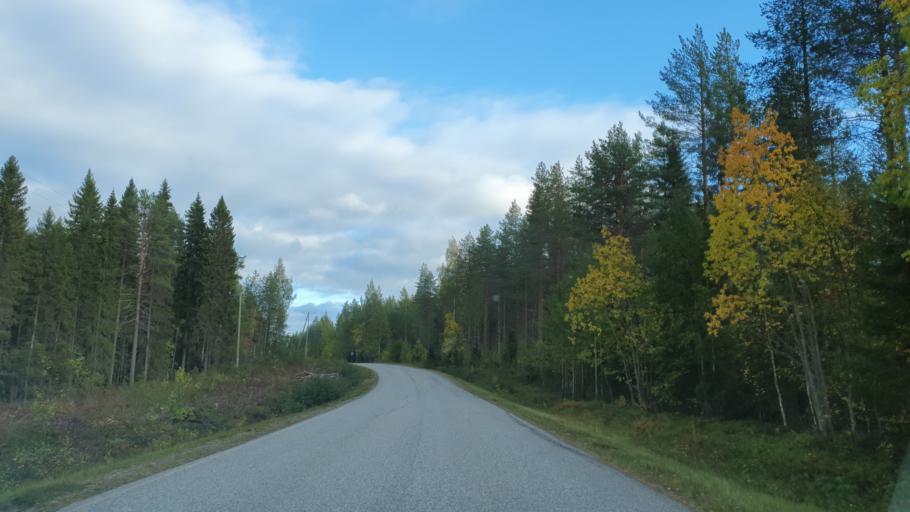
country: FI
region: Kainuu
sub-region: Kehys-Kainuu
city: Kuhmo
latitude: 63.9302
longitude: 29.9948
